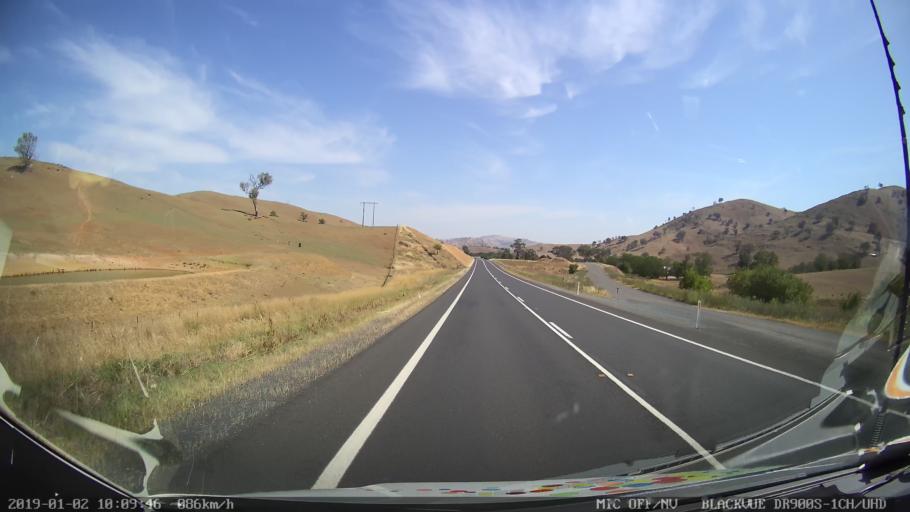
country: AU
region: New South Wales
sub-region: Gundagai
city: Gundagai
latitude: -35.1130
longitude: 148.0976
